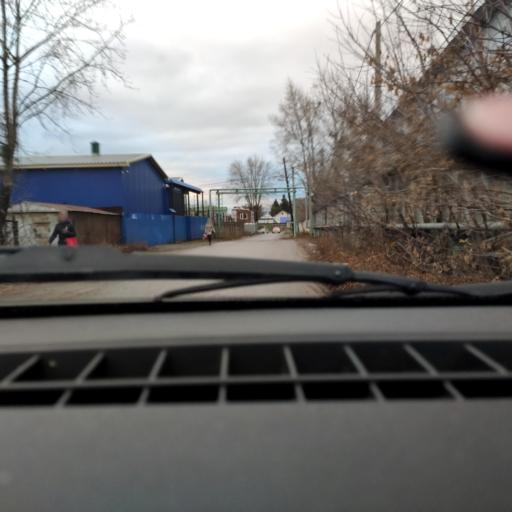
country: RU
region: Bashkortostan
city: Ufa
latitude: 54.8249
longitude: 56.1016
